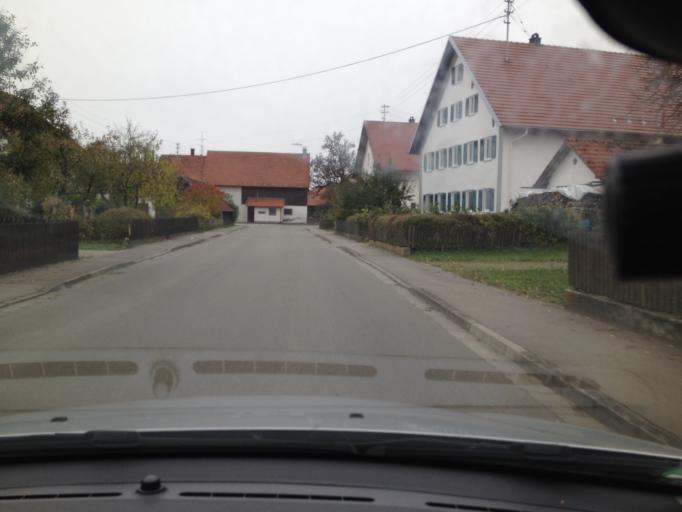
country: DE
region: Bavaria
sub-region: Swabia
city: Ettringen
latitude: 48.1346
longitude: 10.6657
